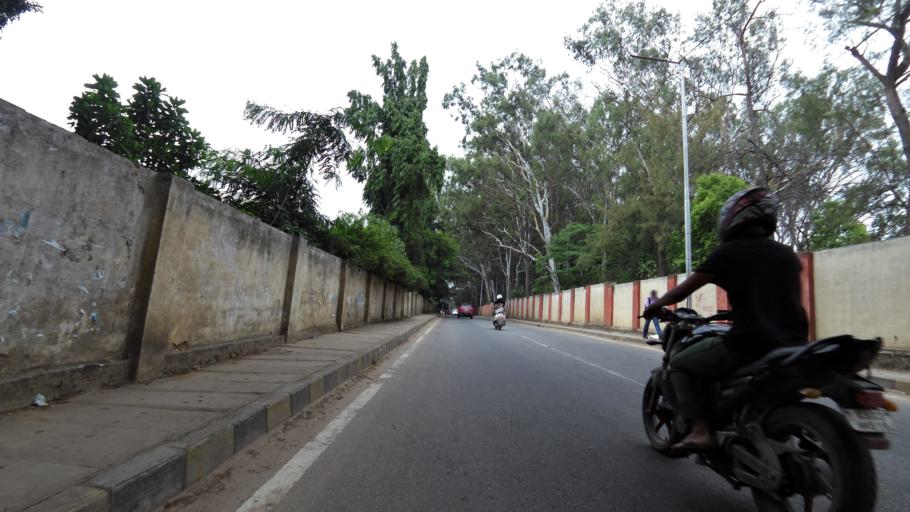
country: IN
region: Karnataka
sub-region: Bangalore Urban
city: Bangalore
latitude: 12.9869
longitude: 77.6428
